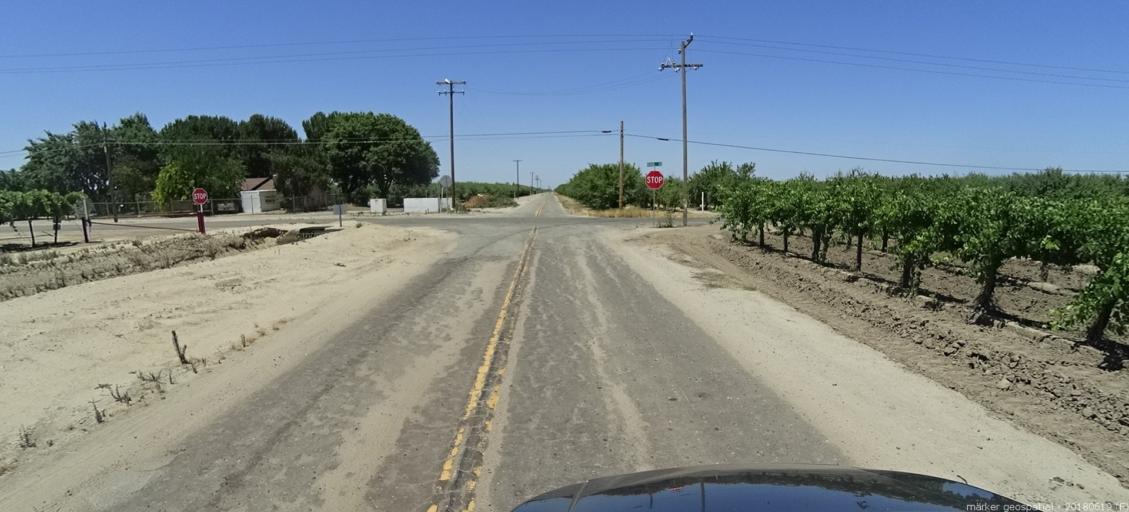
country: US
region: California
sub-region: Madera County
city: Parkwood
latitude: 36.8730
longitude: -120.0917
